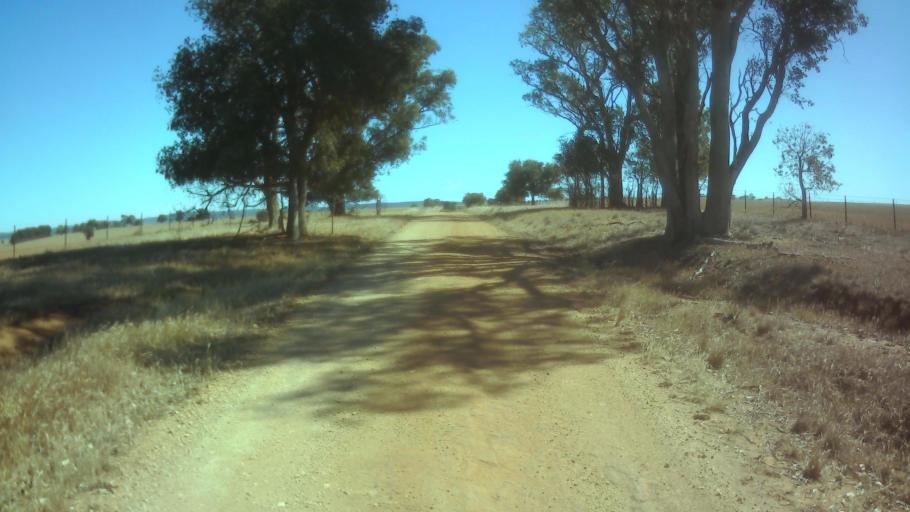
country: AU
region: New South Wales
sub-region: Weddin
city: Grenfell
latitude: -33.9768
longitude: 148.3426
